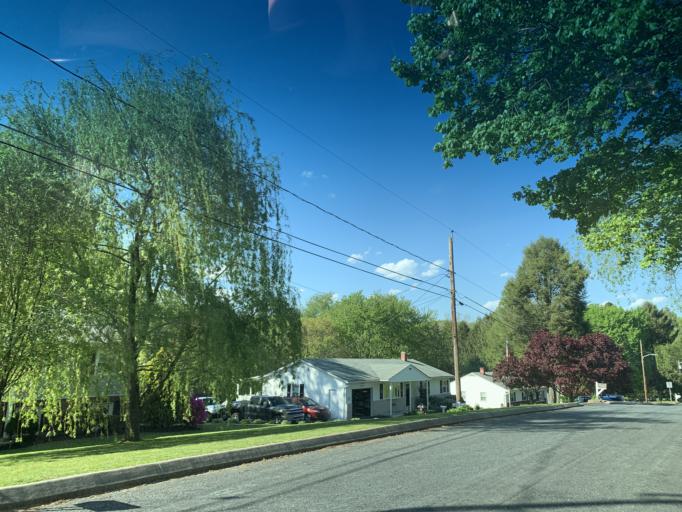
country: US
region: Maryland
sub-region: Harford County
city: Aberdeen
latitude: 39.5387
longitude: -76.2078
